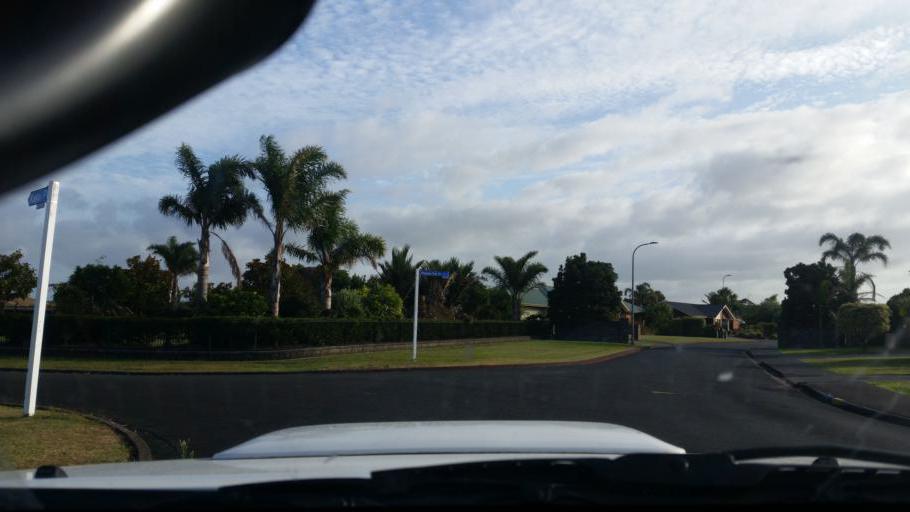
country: NZ
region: Northland
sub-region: Kaipara District
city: Dargaville
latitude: -35.9280
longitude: 173.8645
